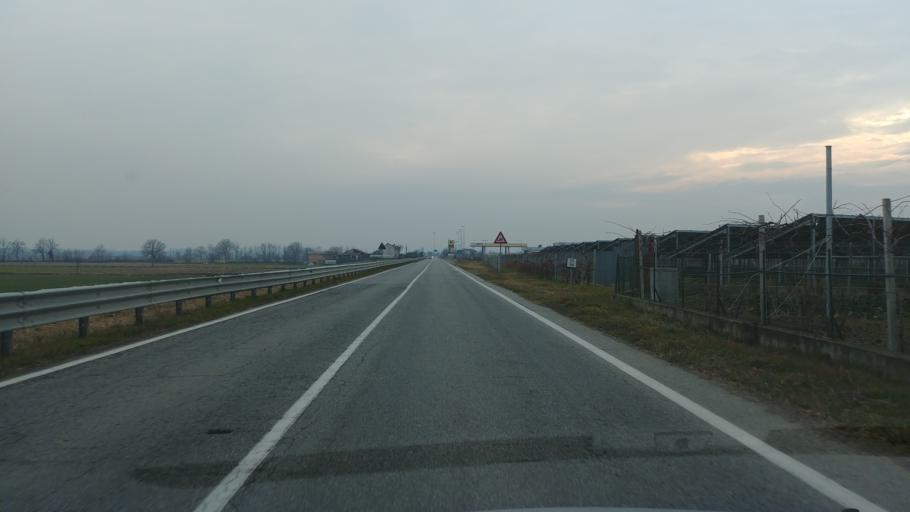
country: IT
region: Piedmont
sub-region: Provincia di Cuneo
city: Castelletto Stura
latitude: 44.4661
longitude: 7.6337
